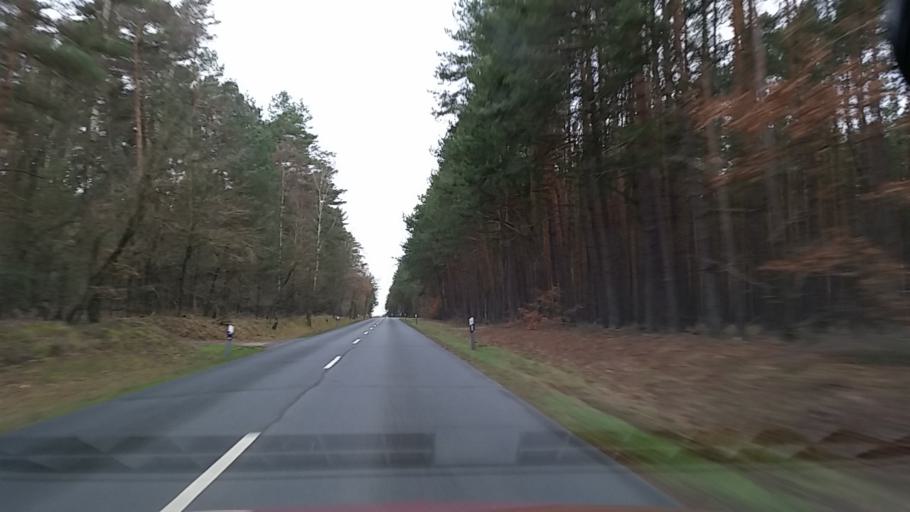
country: DE
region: Lower Saxony
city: Wieren
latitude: 52.8832
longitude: 10.6190
